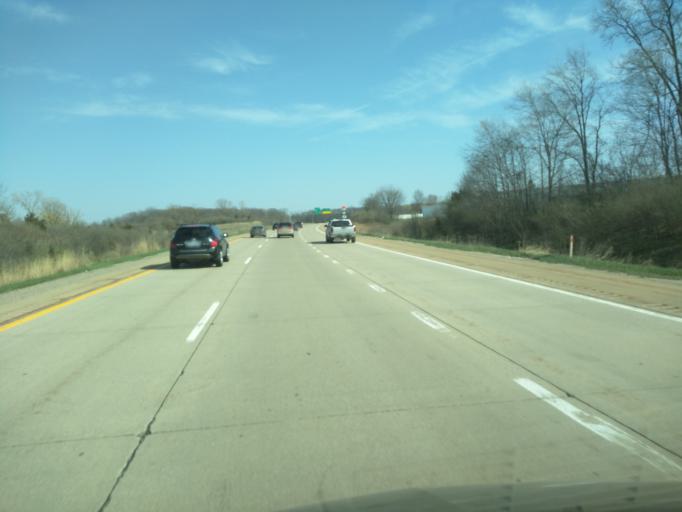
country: US
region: Michigan
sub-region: Kent County
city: Forest Hills
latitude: 42.9063
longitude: -85.5269
